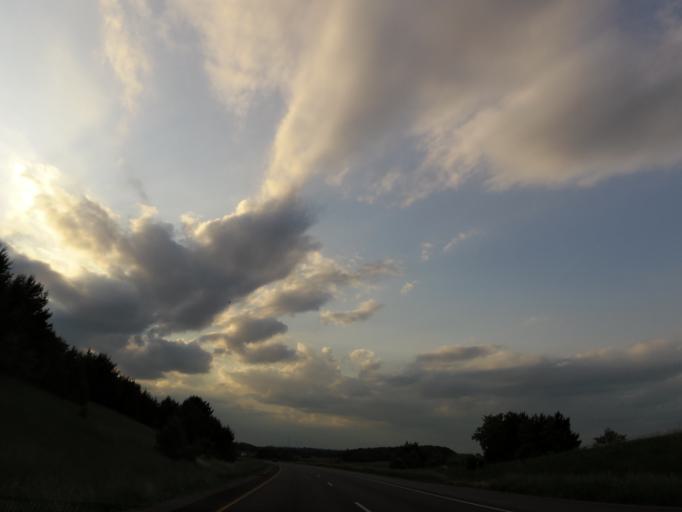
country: US
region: Wisconsin
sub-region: Trempealeau County
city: Osseo
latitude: 44.4474
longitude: -91.0804
